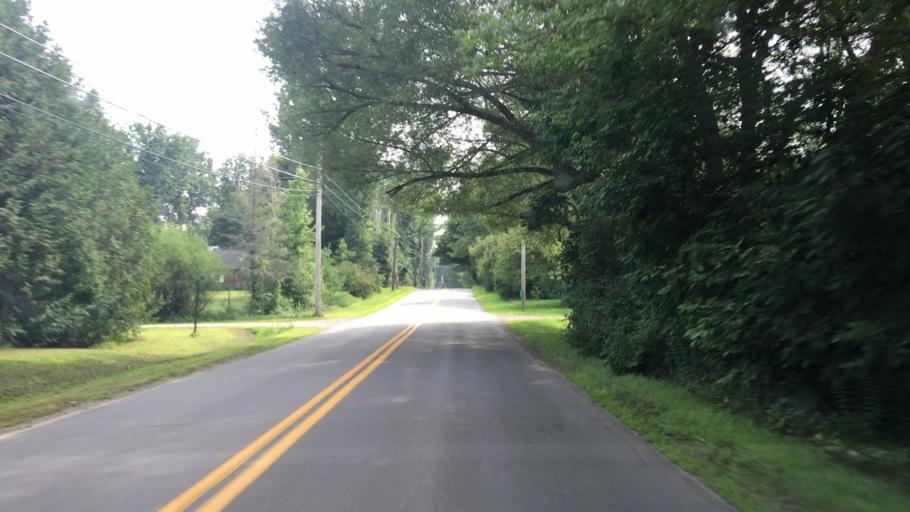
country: US
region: Maine
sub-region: Lincoln County
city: Jefferson
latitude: 44.1784
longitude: -69.4623
